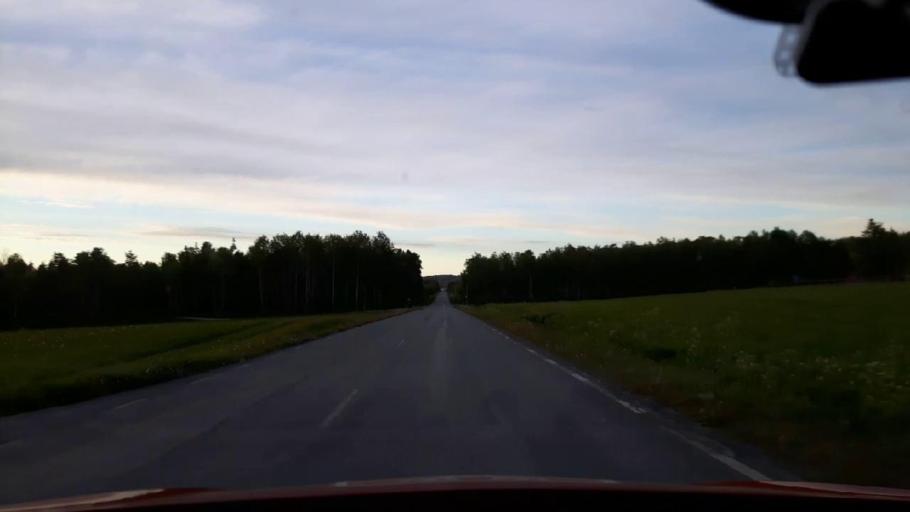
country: SE
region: Jaemtland
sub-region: OEstersunds Kommun
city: Ostersund
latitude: 63.1377
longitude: 14.4639
